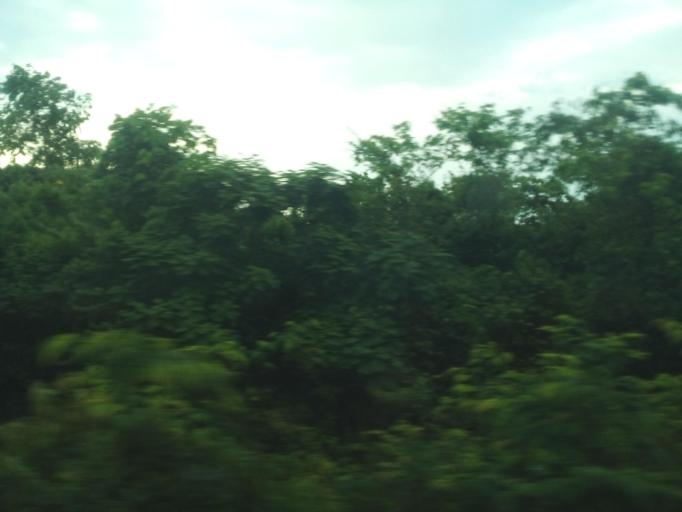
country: BR
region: Maranhao
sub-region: Imperatriz
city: Imperatriz
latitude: -4.6832
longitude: -47.2721
